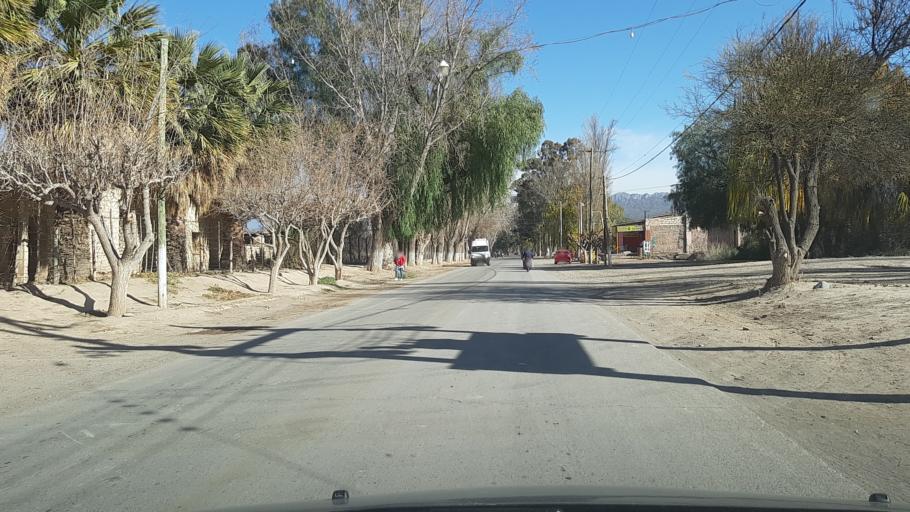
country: AR
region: San Juan
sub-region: Departamento de Zonda
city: Zonda
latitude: -31.4611
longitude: -68.7325
